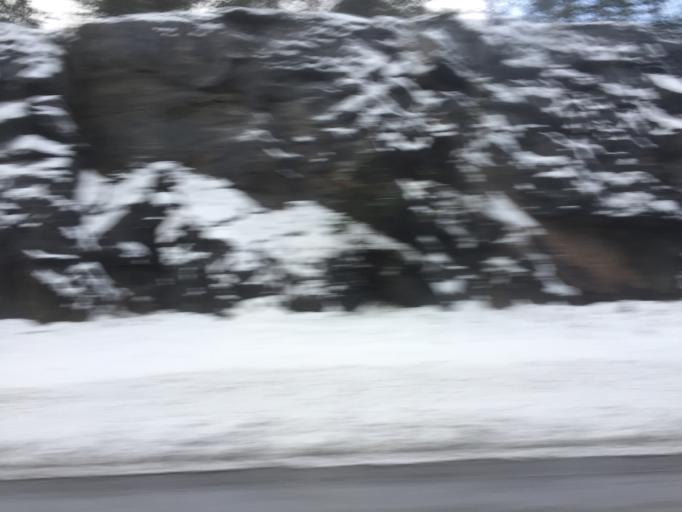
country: NO
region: Akershus
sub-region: Oppegard
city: Kolbotn
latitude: 59.8362
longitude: 10.7786
